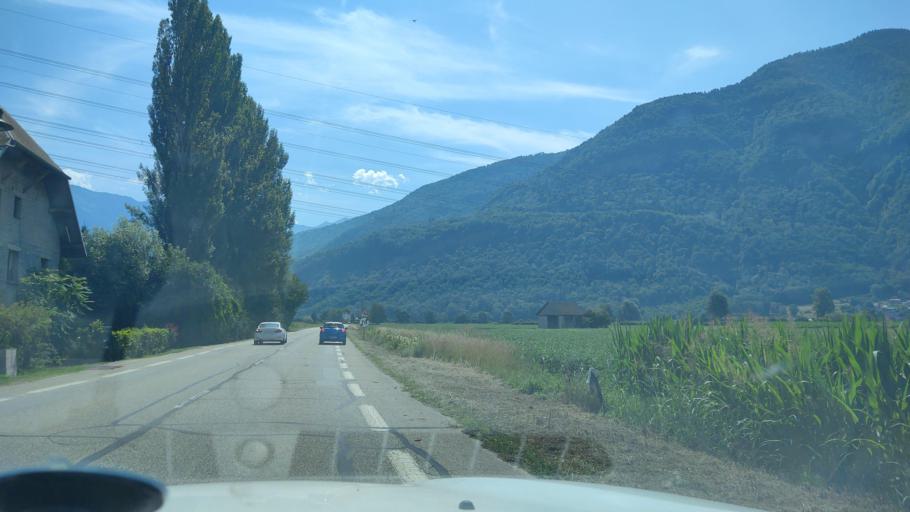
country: FR
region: Rhone-Alpes
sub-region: Departement de la Savoie
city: Aiton
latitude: 45.5520
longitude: 6.2259
